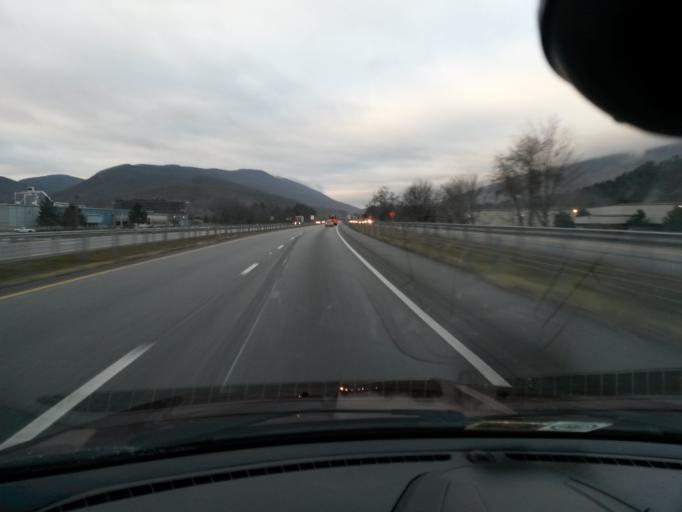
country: US
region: Virginia
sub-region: Alleghany County
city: Clifton Forge
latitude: 37.7966
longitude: -79.8757
